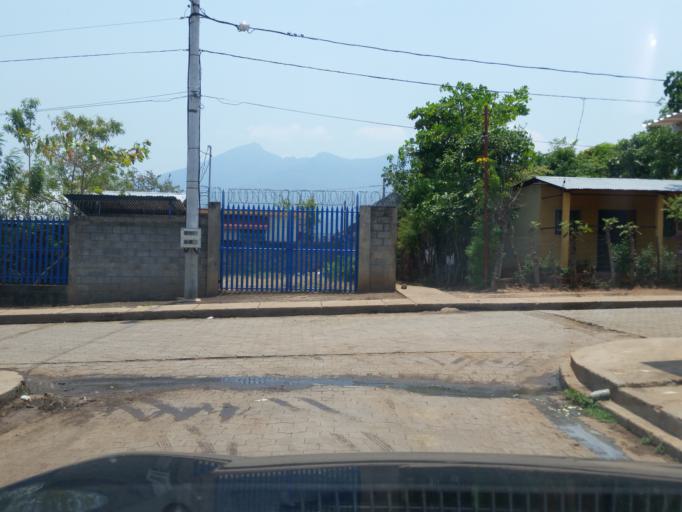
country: NI
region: Granada
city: Granada
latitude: 11.9098
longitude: -85.9583
